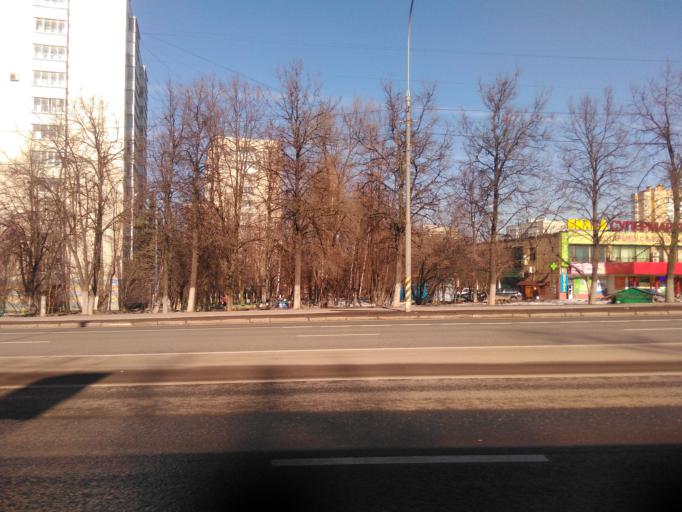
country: RU
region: Moscow
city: Zyuzino
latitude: 55.6501
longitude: 37.5592
